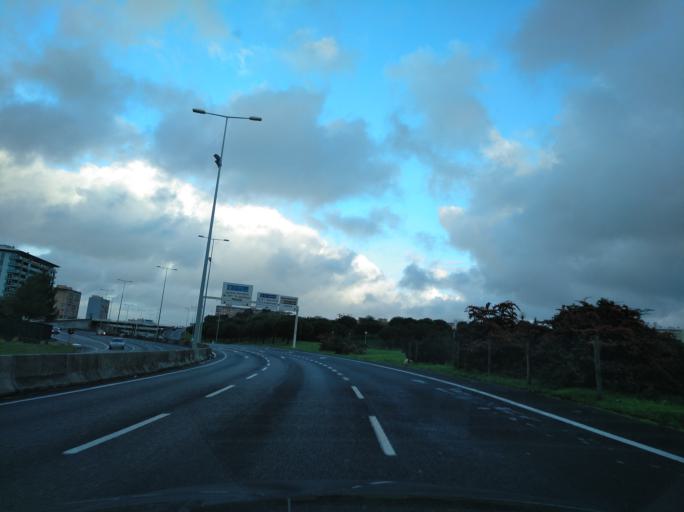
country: PT
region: Lisbon
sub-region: Lisbon
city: Lisbon
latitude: 38.7468
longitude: -9.1252
